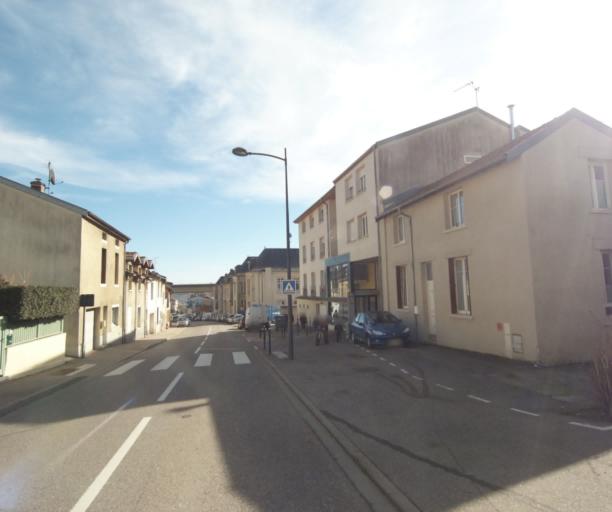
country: FR
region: Lorraine
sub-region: Departement de Meurthe-et-Moselle
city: Maxeville
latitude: 48.7131
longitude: 6.1591
